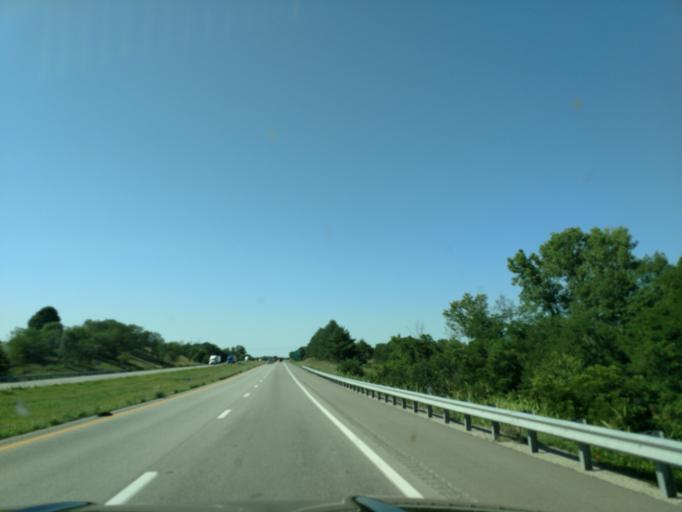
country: US
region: Missouri
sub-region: Andrew County
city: Country Club Village
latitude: 39.8380
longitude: -94.8052
